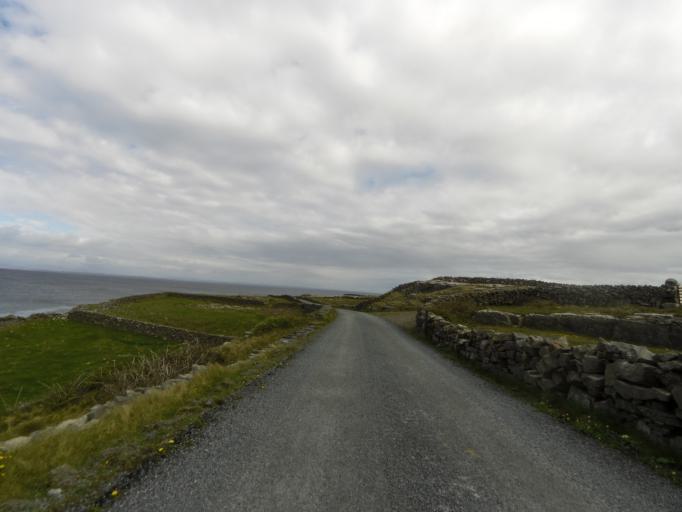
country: IE
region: Connaught
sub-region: County Galway
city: Clifden
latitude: 53.1345
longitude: -9.7415
